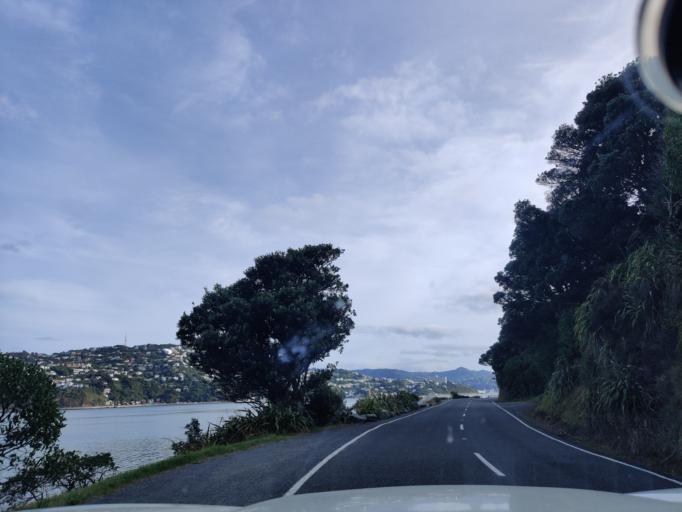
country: NZ
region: Wellington
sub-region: Wellington City
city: Wellington
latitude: -41.3010
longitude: 174.8179
